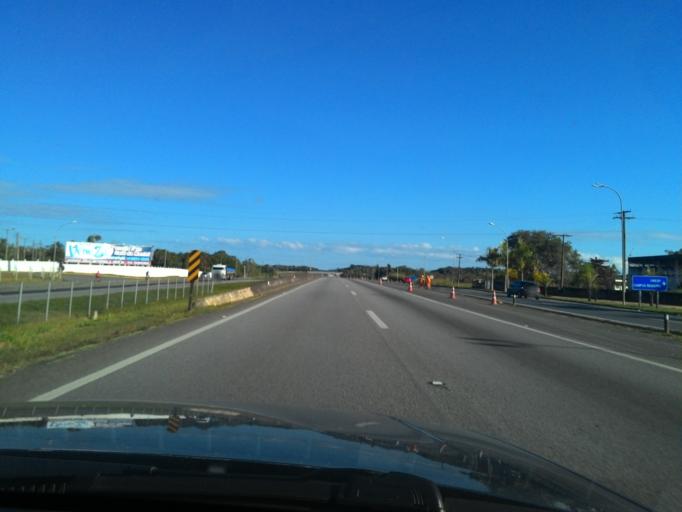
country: BR
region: Sao Paulo
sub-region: Registro
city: Registro
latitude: -24.5314
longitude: -47.8572
